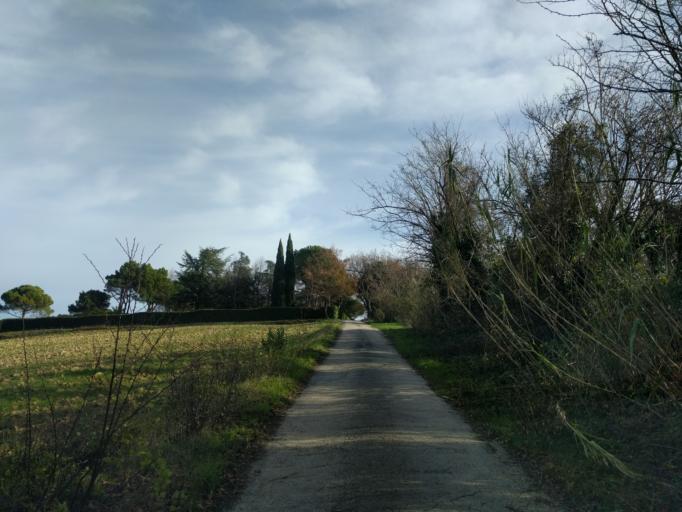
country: IT
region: The Marches
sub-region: Provincia di Pesaro e Urbino
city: Cuccurano
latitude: 43.8097
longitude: 12.9556
